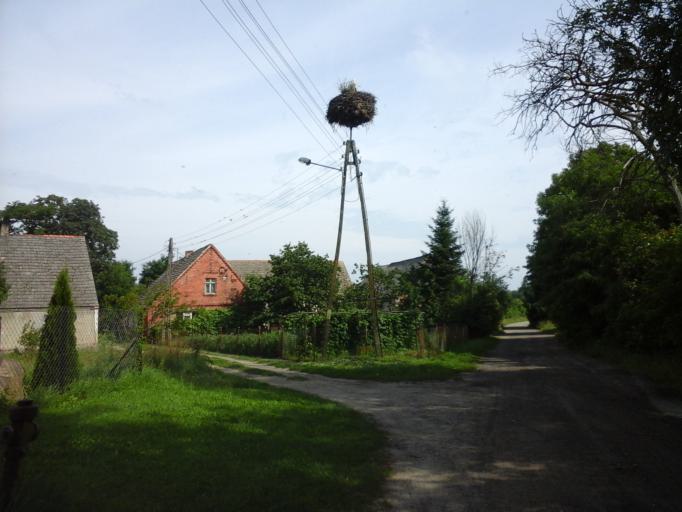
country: PL
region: West Pomeranian Voivodeship
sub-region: Powiat choszczenski
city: Bierzwnik
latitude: 53.1126
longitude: 15.6224
